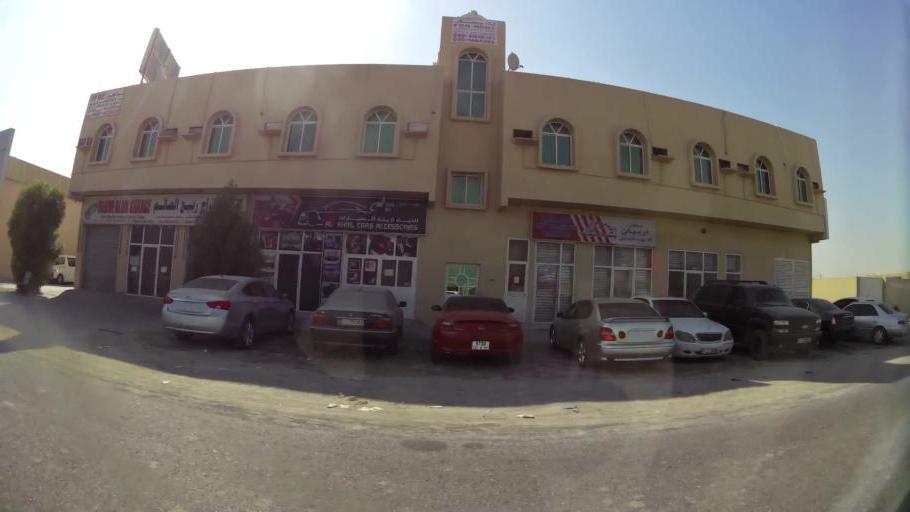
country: AE
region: Ajman
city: Ajman
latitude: 25.4380
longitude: 55.5106
